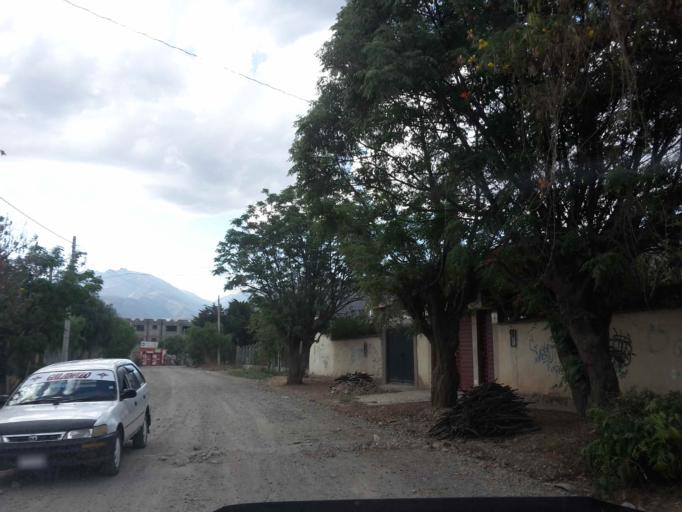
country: BO
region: Cochabamba
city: Cochabamba
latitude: -17.3347
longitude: -66.2173
